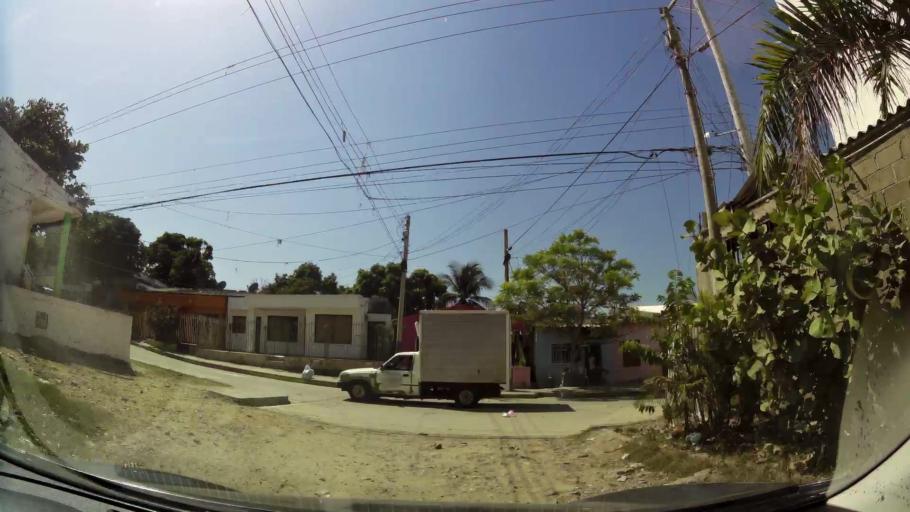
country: CO
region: Bolivar
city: Cartagena
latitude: 10.3904
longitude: -75.5137
